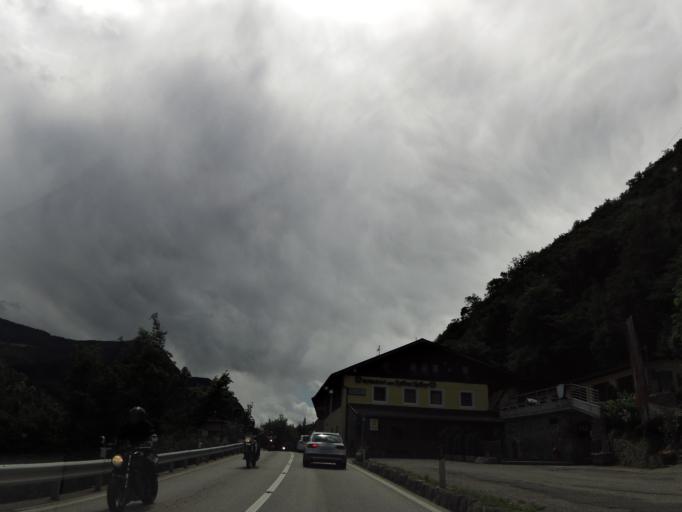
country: IT
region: Trentino-Alto Adige
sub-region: Bolzano
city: Barbiano
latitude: 46.6122
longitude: 11.5337
